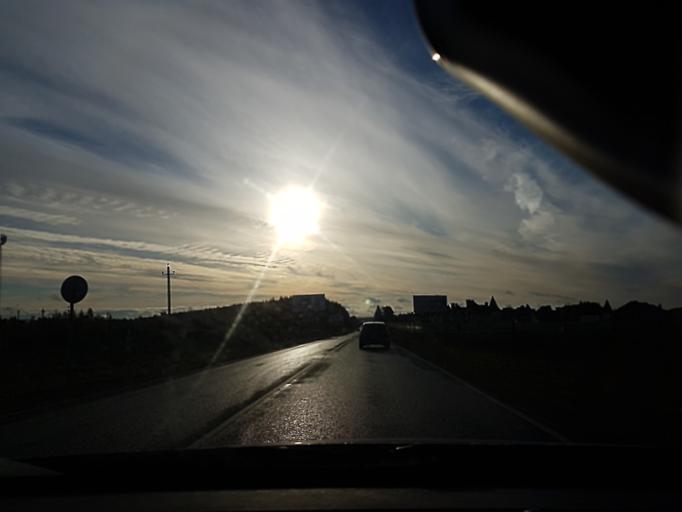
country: RU
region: Moskovskaya
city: Rozhdestveno
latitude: 55.8282
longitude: 37.0356
